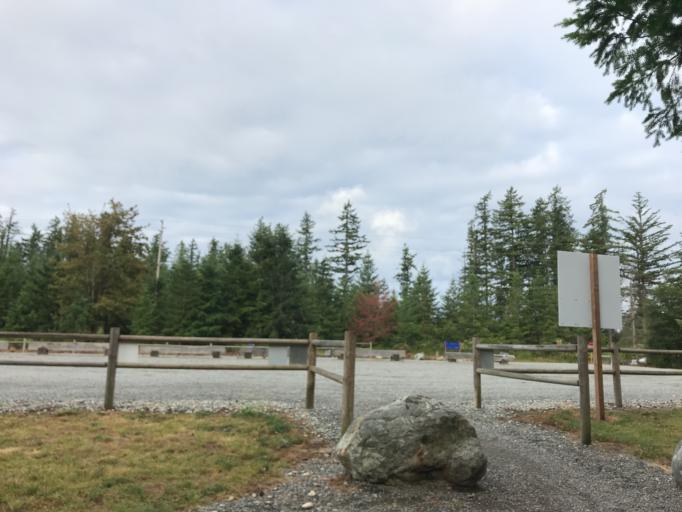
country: US
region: Washington
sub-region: King County
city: Black Diamond
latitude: 47.3364
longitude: -122.0128
